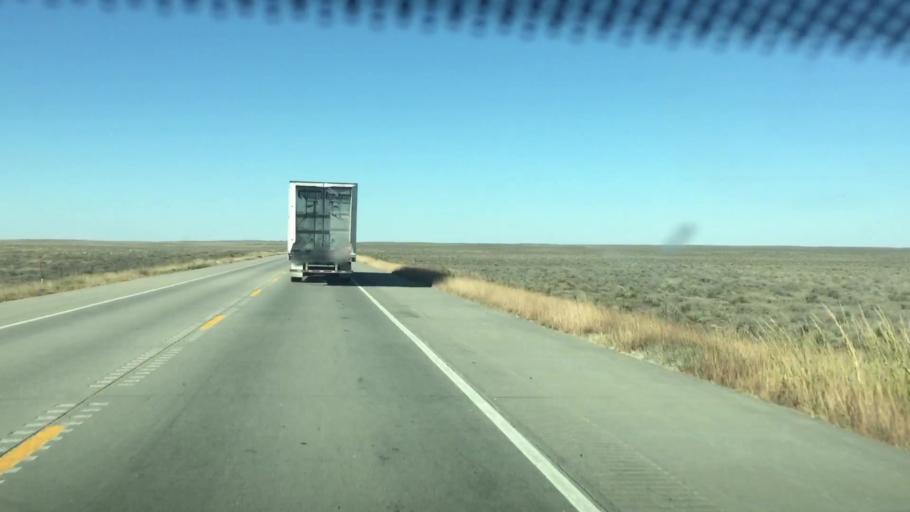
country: US
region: Colorado
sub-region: Kiowa County
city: Eads
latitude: 38.5510
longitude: -102.7859
